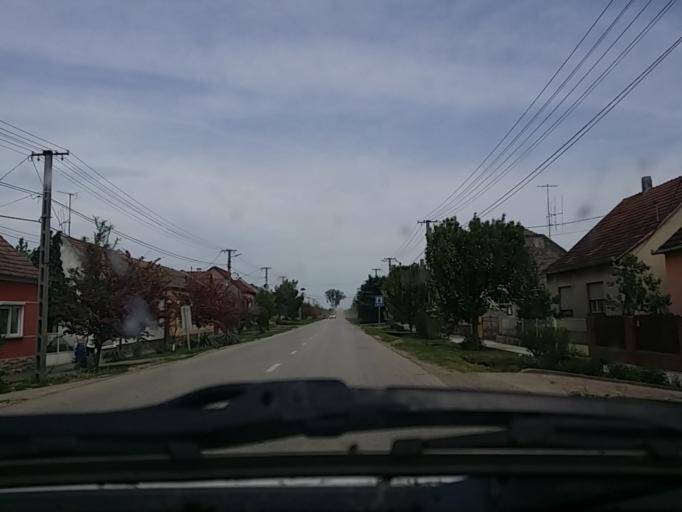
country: HU
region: Baranya
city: Sellye
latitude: 45.8746
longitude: 17.8599
